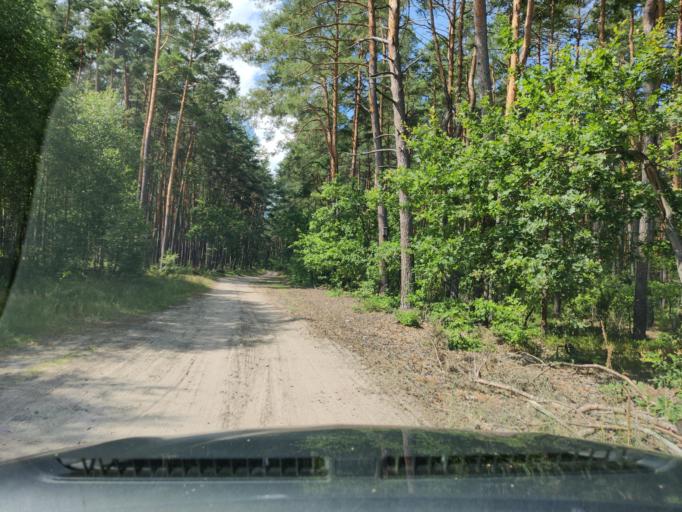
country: PL
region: Masovian Voivodeship
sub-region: Powiat pultuski
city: Obryte
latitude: 52.7426
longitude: 21.1749
